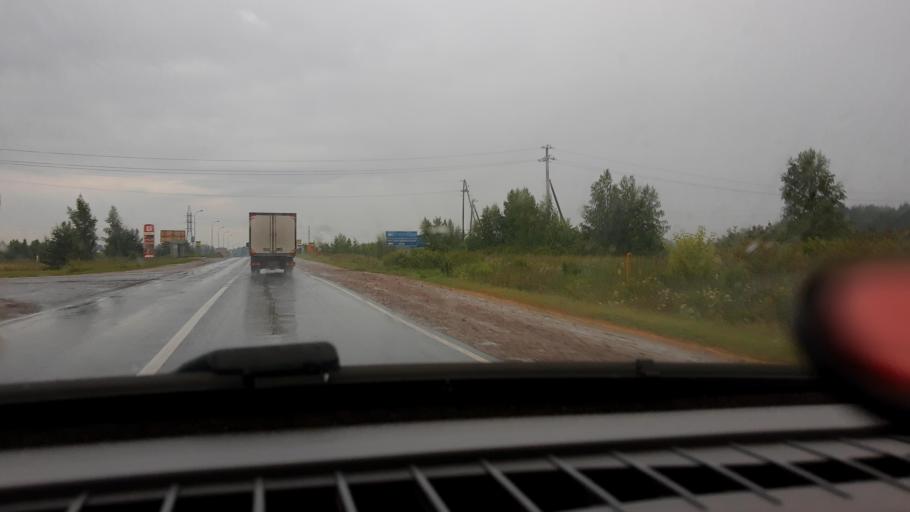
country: RU
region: Nizjnij Novgorod
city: Gorodets
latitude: 56.6857
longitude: 43.4672
